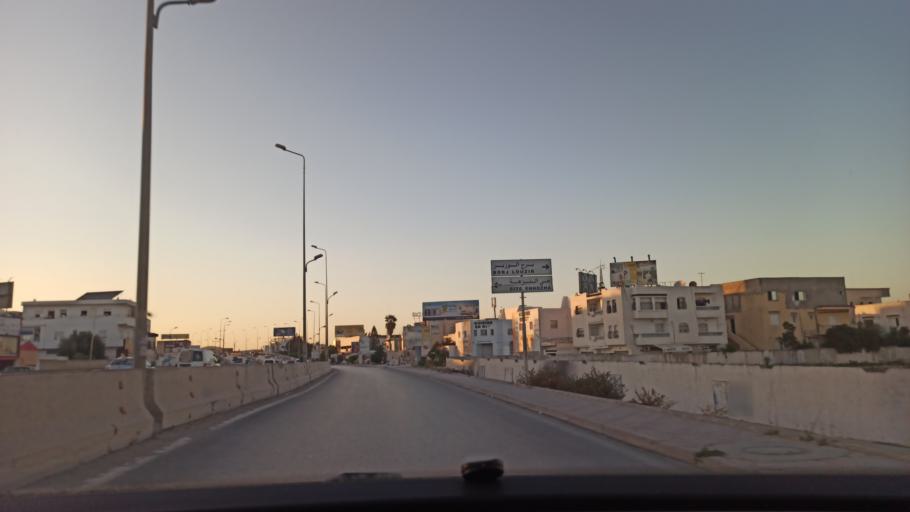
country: TN
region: Ariana
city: Ariana
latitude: 36.8615
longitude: 10.2024
